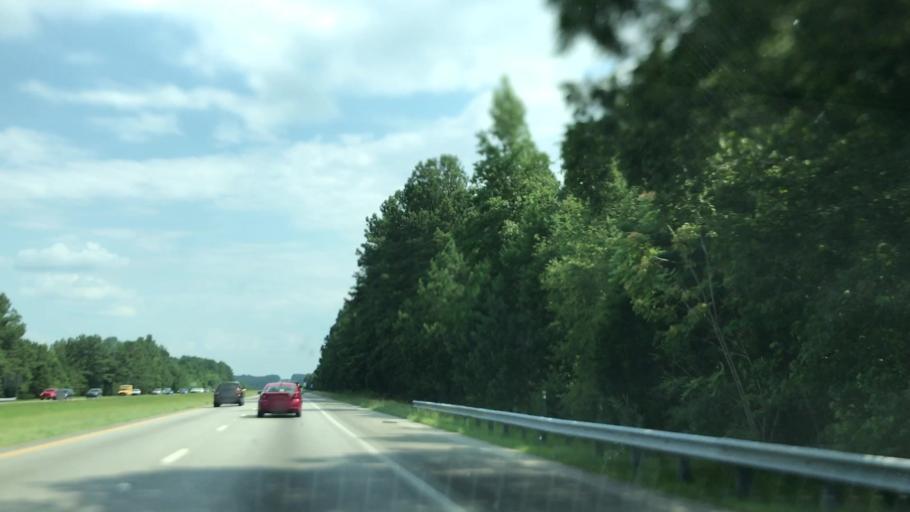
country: US
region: South Carolina
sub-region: Chester County
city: Great Falls
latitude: 34.6032
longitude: -81.0183
